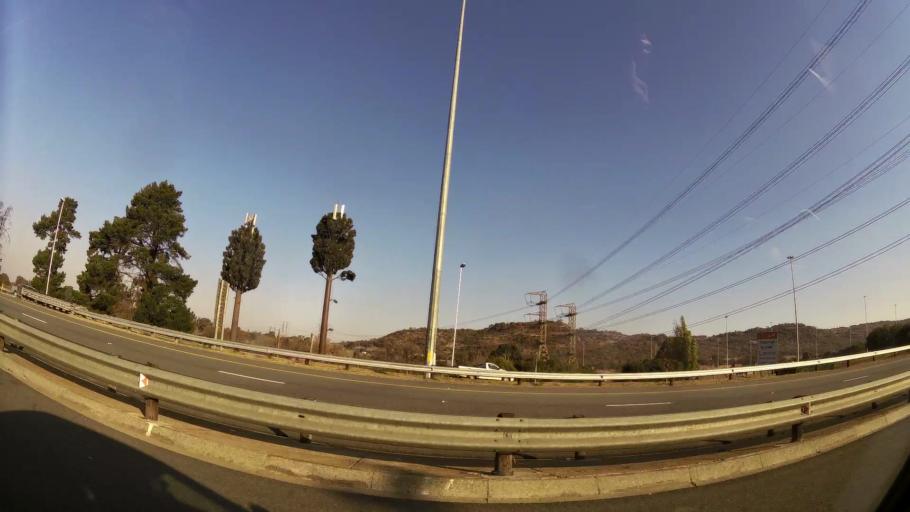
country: ZA
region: Gauteng
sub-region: City of Johannesburg Metropolitan Municipality
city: Johannesburg
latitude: -26.2637
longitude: 28.0980
